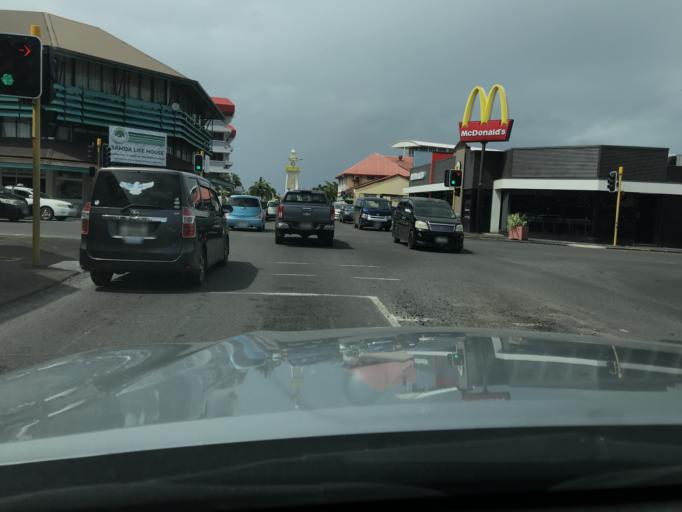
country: WS
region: Tuamasaga
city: Apia
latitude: -13.8318
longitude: -171.7690
